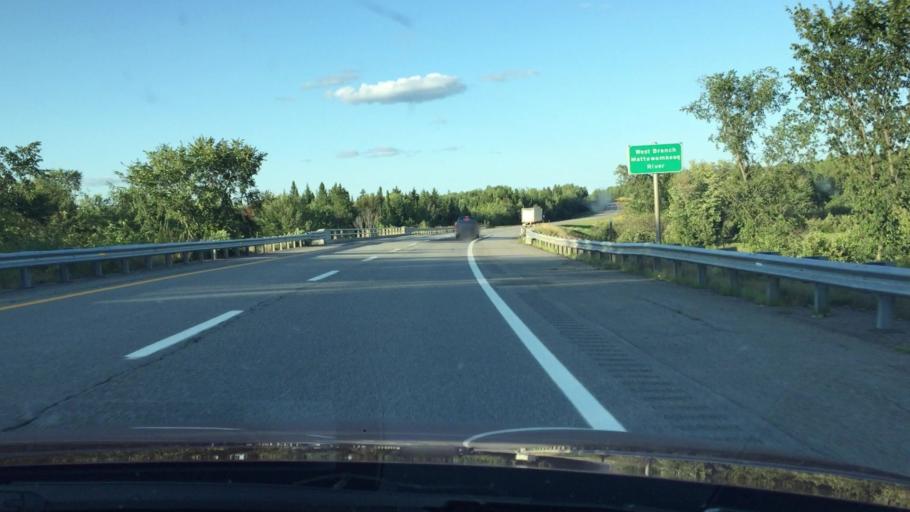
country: US
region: Maine
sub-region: Penobscot County
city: Patten
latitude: 46.0246
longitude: -68.2863
